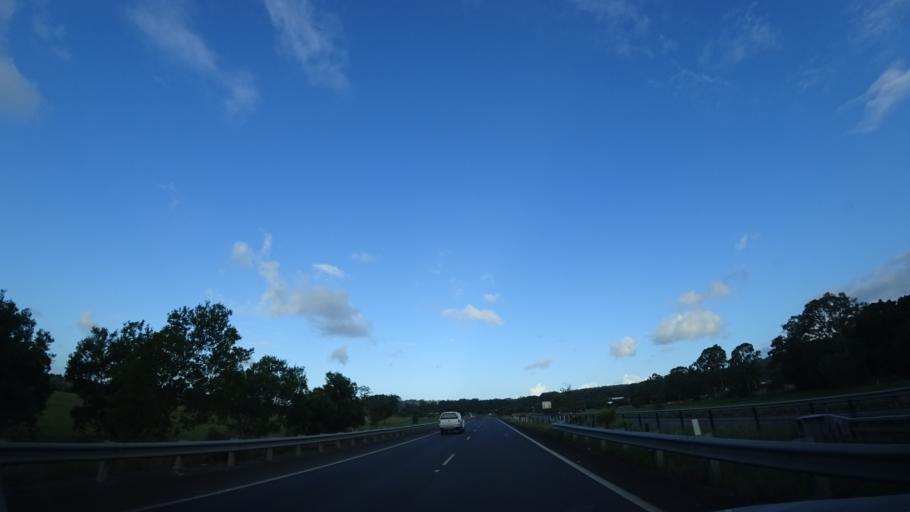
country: AU
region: Queensland
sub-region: Sunshine Coast
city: Woombye
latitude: -26.6715
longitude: 153.0113
